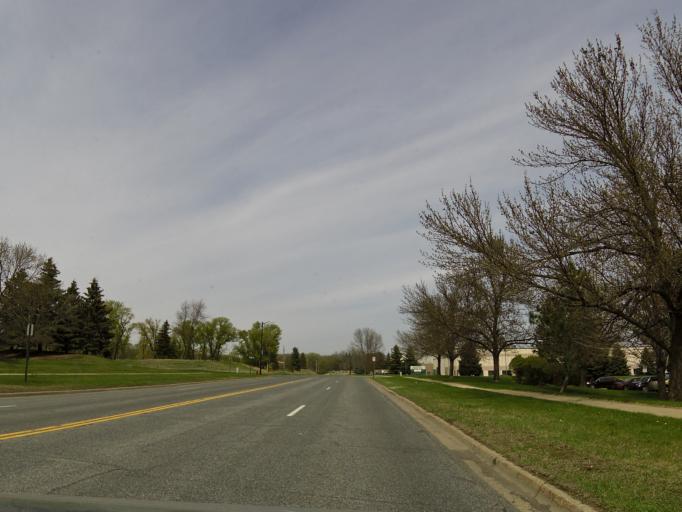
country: US
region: Minnesota
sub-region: Scott County
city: Savage
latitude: 44.8108
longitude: -93.3685
